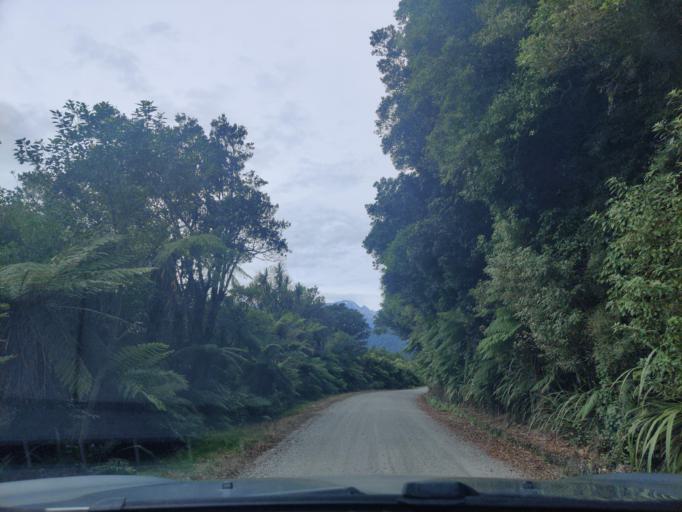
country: NZ
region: West Coast
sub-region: Westland District
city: Hokitika
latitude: -43.2899
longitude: 170.4053
